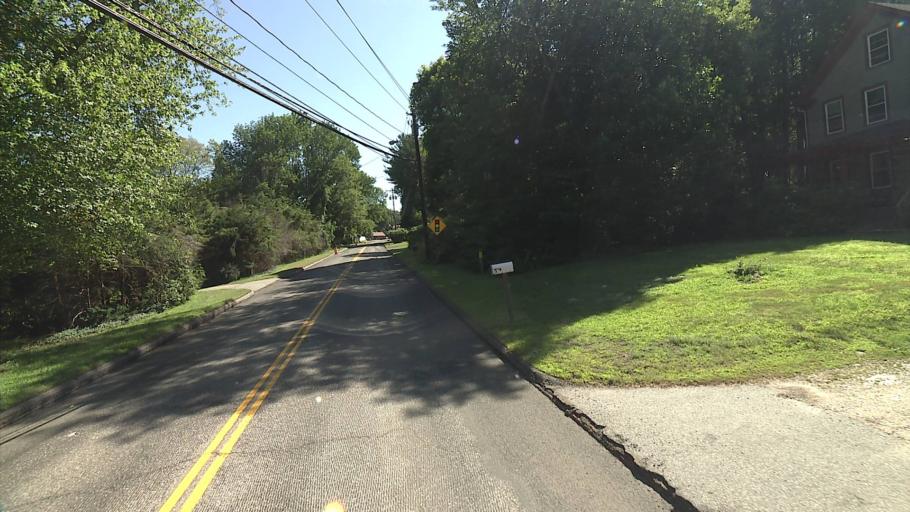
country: US
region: Connecticut
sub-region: Middlesex County
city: East Hampton
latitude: 41.5661
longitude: -72.4994
